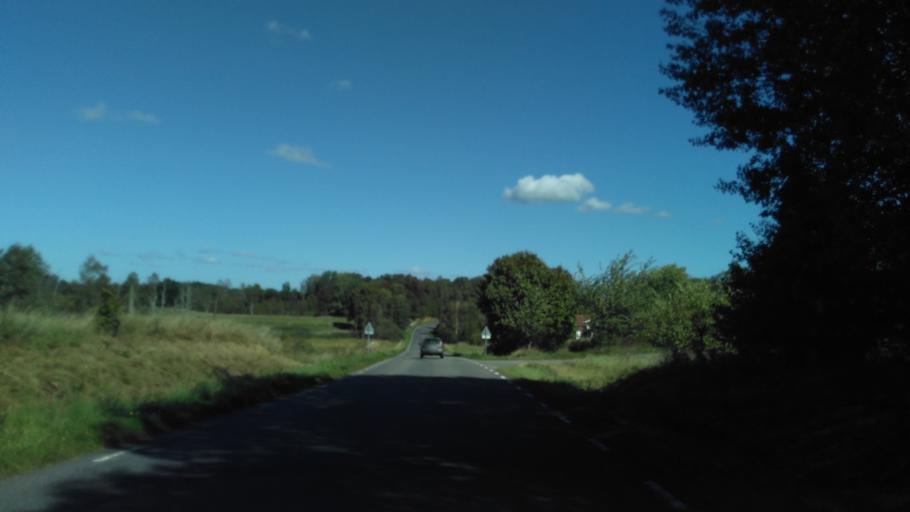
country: SE
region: Vaestra Goetaland
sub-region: Skara Kommun
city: Axvall
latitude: 58.4353
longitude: 13.6467
